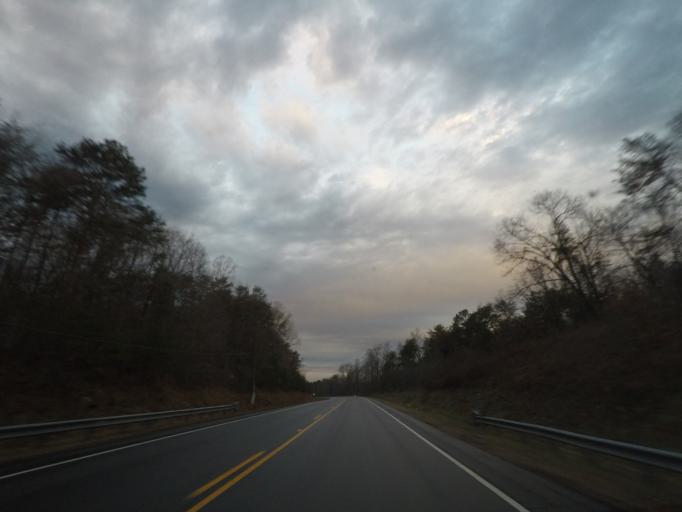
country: US
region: North Carolina
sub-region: Caswell County
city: Yanceyville
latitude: 36.4047
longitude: -79.2983
